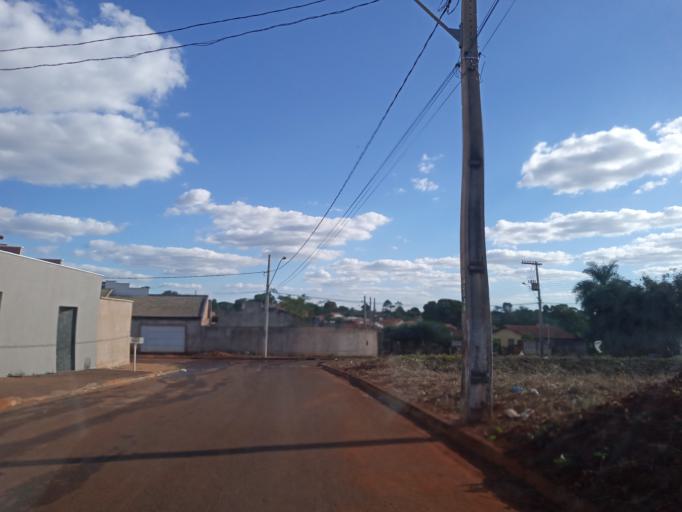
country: BR
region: Minas Gerais
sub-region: Ituiutaba
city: Ituiutaba
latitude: -18.9586
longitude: -49.4497
